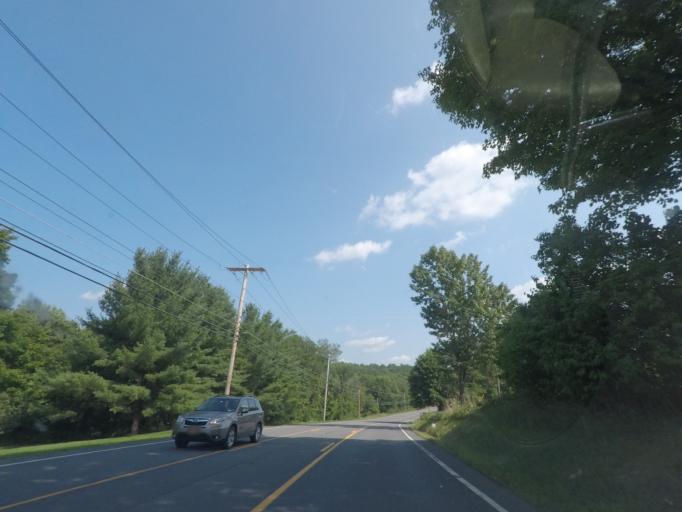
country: US
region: New York
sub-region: Rensselaer County
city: Nassau
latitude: 42.5378
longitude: -73.6620
